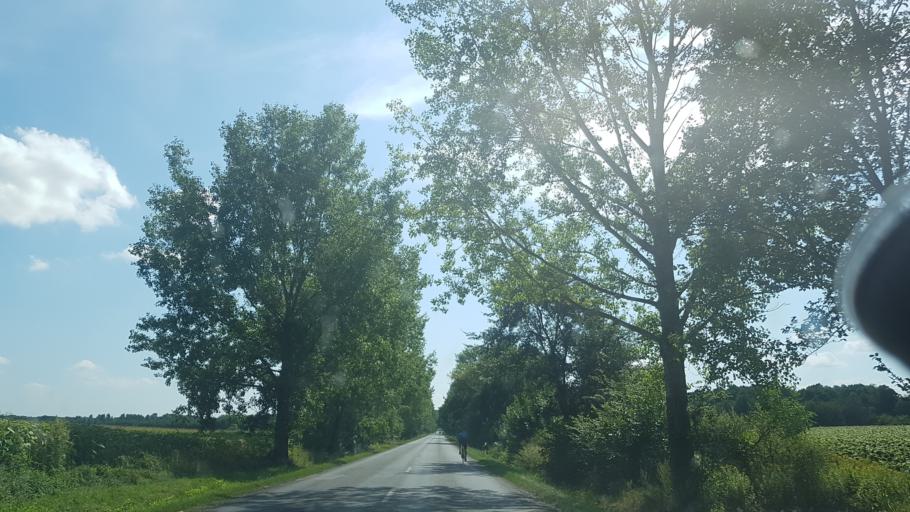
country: HU
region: Somogy
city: Segesd
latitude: 46.3757
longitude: 17.3634
